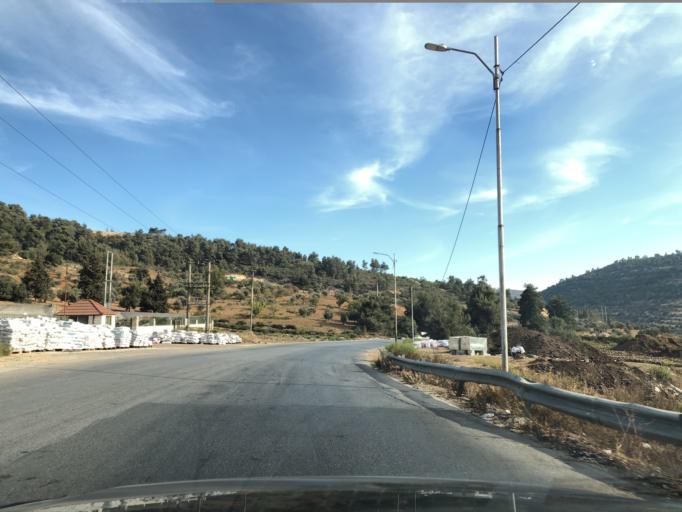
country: JO
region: Irbid
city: Sakib
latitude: 32.2860
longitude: 35.7941
